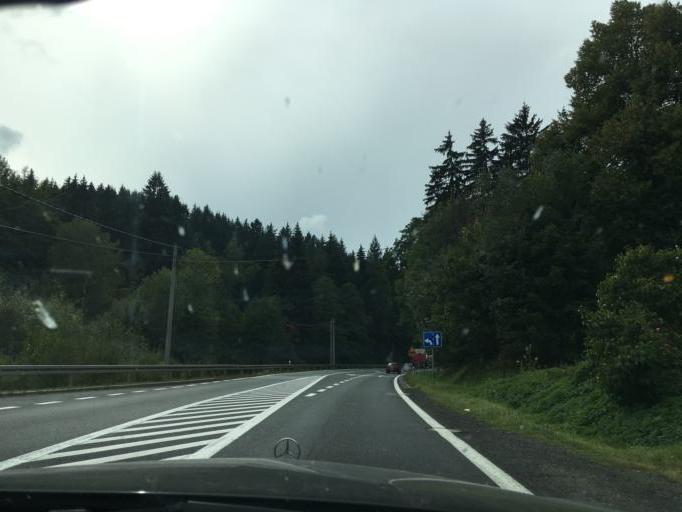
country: PL
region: Lower Silesian Voivodeship
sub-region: Powiat klodzki
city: Duszniki-Zdroj
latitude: 50.3944
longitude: 16.3680
